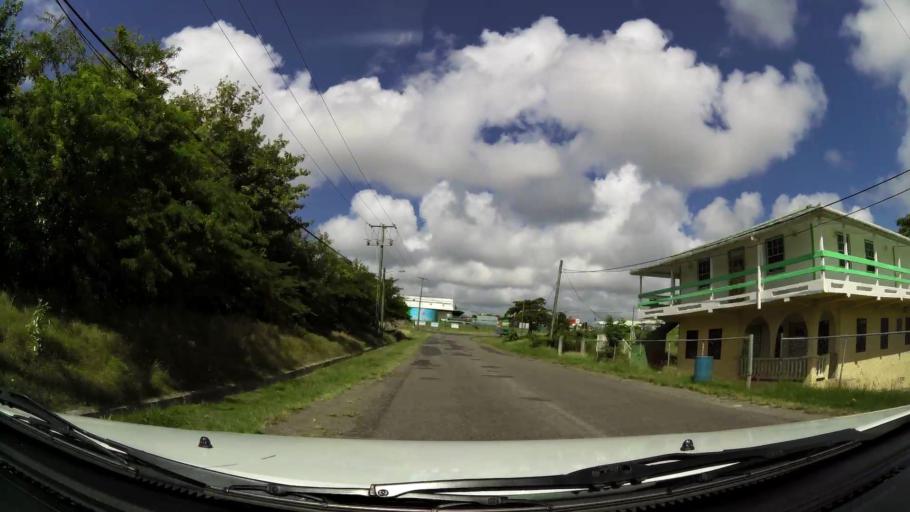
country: LC
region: Laborie Quarter
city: Laborie
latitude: 13.7482
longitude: -60.9704
